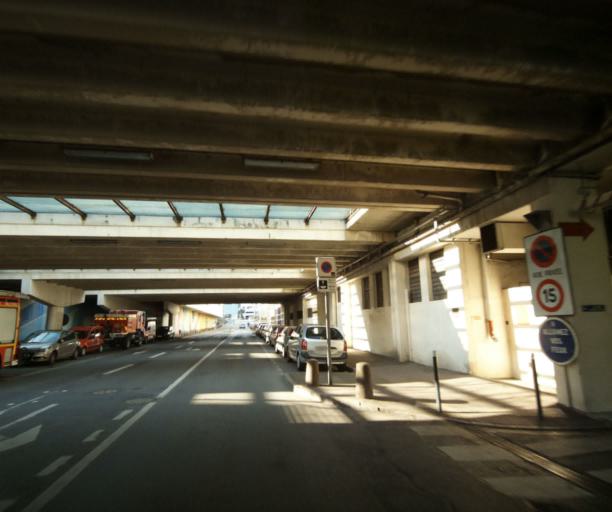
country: FR
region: Ile-de-France
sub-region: Departement du Val-d'Oise
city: Cergy
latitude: 49.0360
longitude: 2.0779
